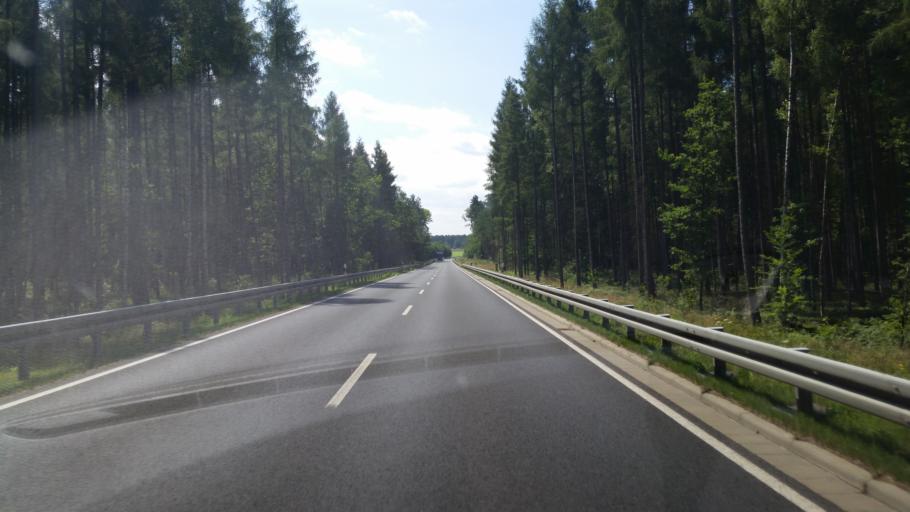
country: DE
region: Saxony
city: Bernsdorf
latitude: 51.3628
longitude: 14.0805
